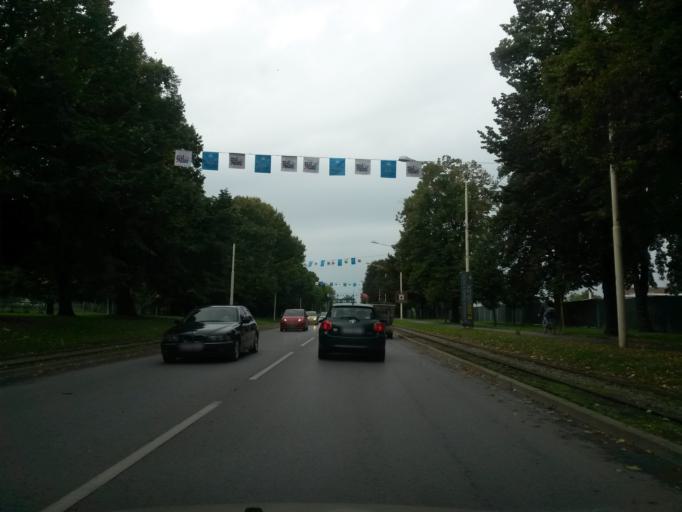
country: HR
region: Osjecko-Baranjska
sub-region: Grad Osijek
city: Osijek
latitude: 45.5590
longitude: 18.7022
